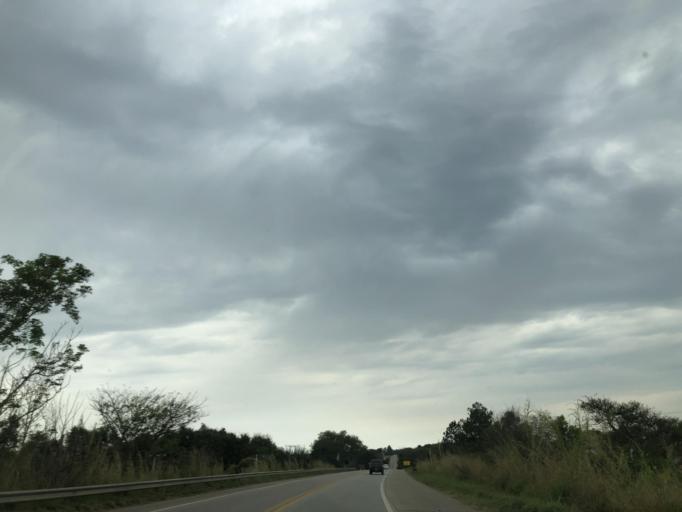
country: BR
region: Sao Paulo
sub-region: Salto De Pirapora
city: Salto de Pirapora
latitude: -23.7093
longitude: -47.6355
